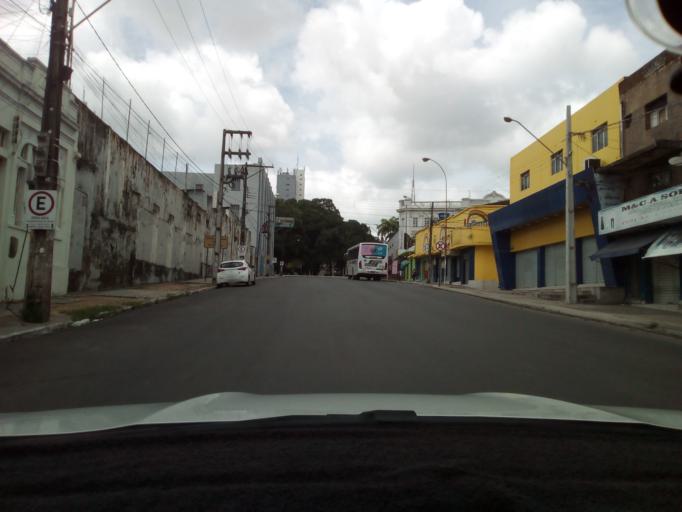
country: BR
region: Paraiba
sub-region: Joao Pessoa
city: Joao Pessoa
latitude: -7.1184
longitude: -34.8883
